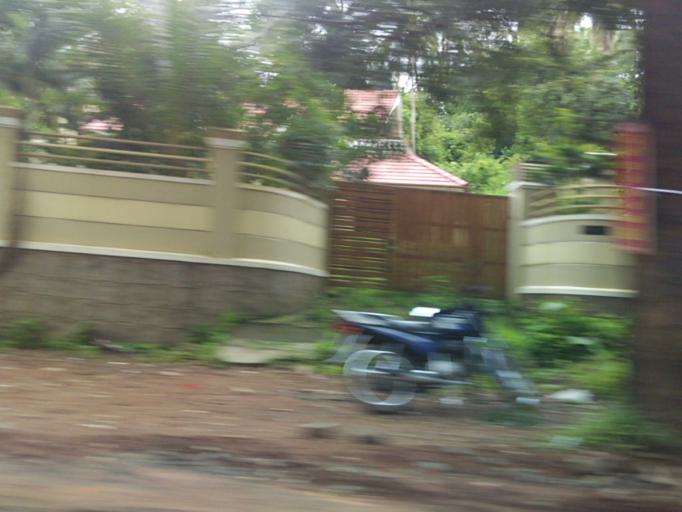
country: IN
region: Kerala
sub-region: Kozhikode
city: Kunnamangalam
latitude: 11.3061
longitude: 75.8853
